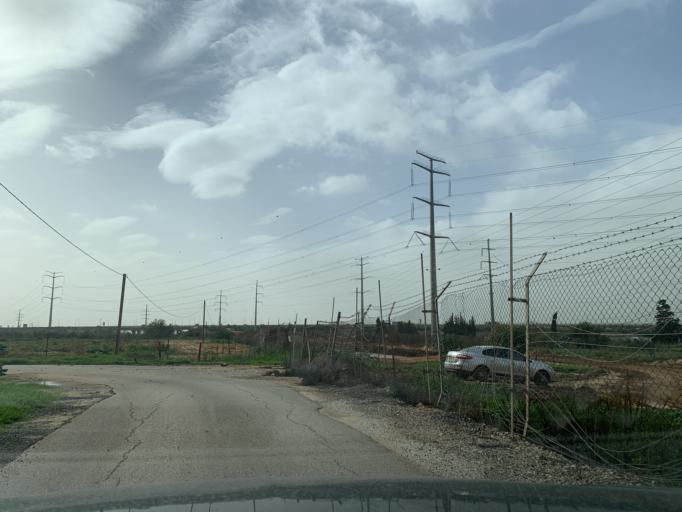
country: IL
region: Central District
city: Jaljulya
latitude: 32.1595
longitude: 34.9386
